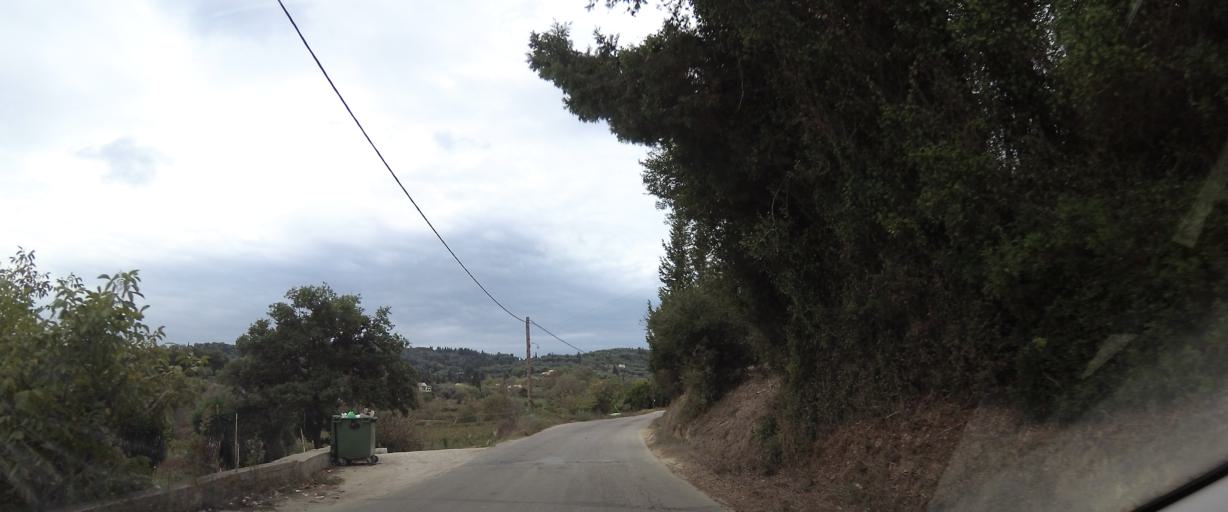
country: GR
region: Ionian Islands
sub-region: Nomos Kerkyras
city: Agios Georgis
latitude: 39.7506
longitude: 19.6853
